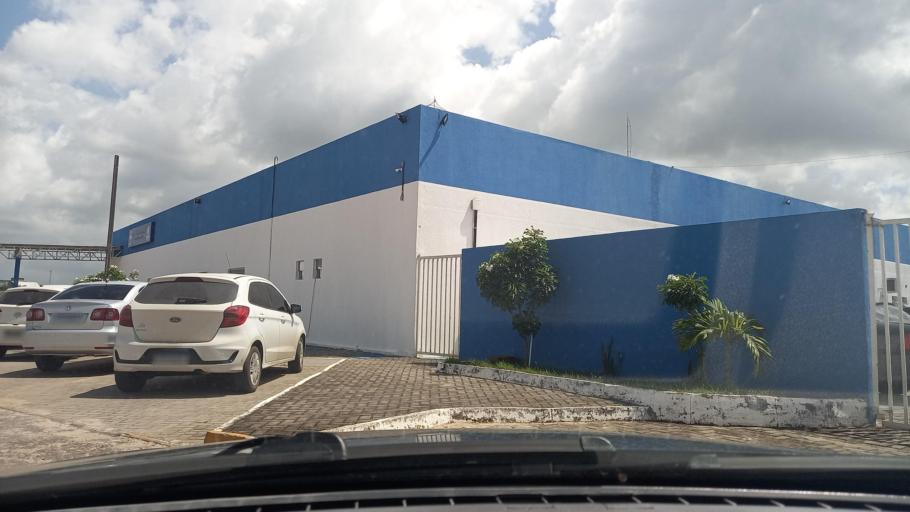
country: BR
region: Pernambuco
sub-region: Goiana
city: Goiana
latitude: -7.5542
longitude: -35.0204
